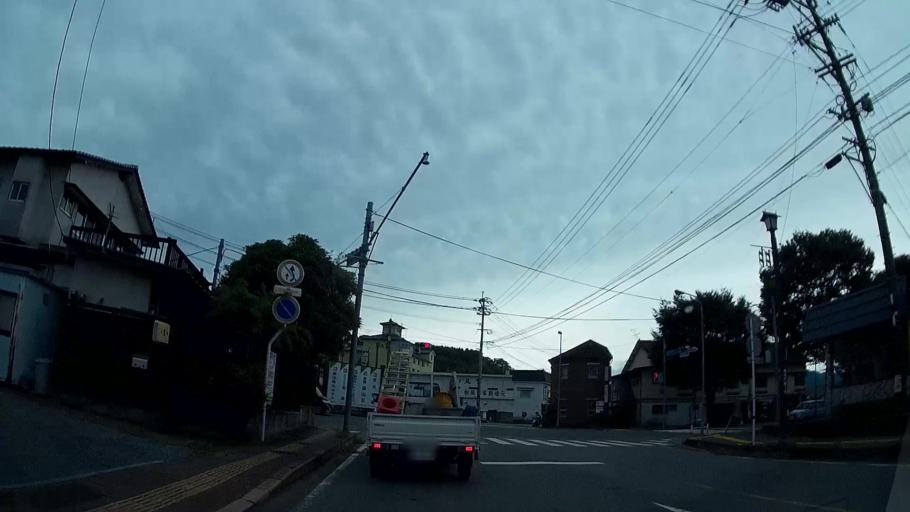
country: JP
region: Kumamoto
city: Kikuchi
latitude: 32.9824
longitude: 130.8153
